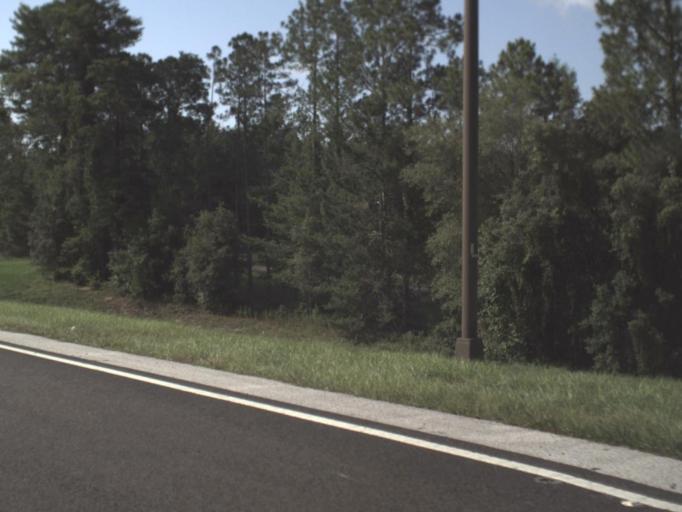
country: US
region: Florida
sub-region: Citrus County
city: Sugarmill Woods
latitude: 28.6878
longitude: -82.4988
